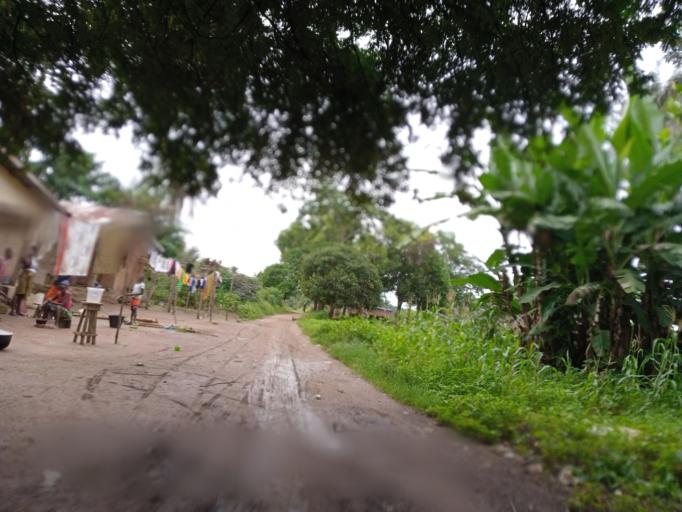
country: SL
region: Northern Province
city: Masoyila
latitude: 8.5862
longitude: -13.1957
